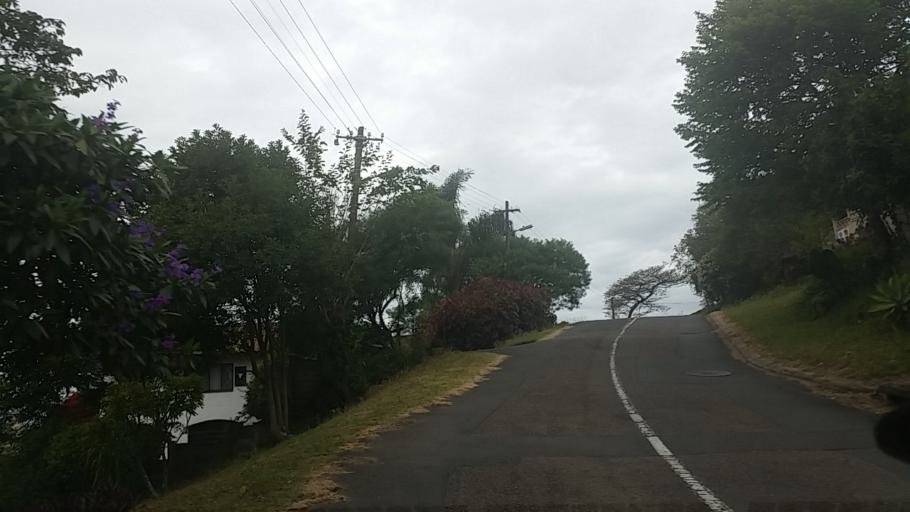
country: ZA
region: KwaZulu-Natal
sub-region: eThekwini Metropolitan Municipality
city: Berea
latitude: -29.8416
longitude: 30.9328
